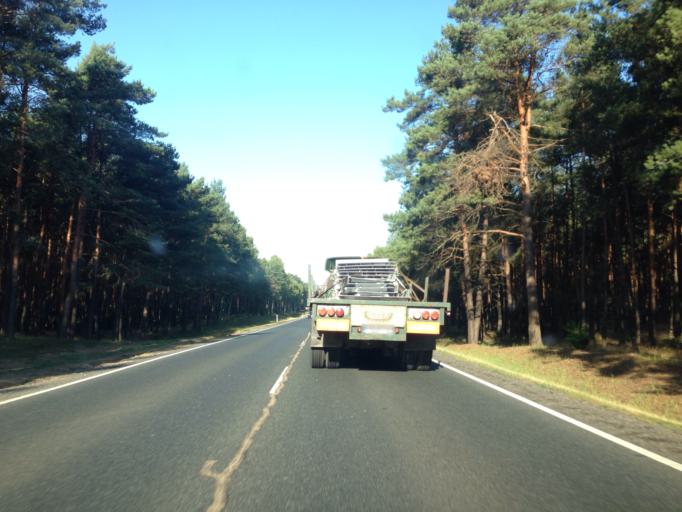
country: PL
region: Kujawsko-Pomorskie
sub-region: Bydgoszcz
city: Bydgoszcz
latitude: 53.0497
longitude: 18.0214
